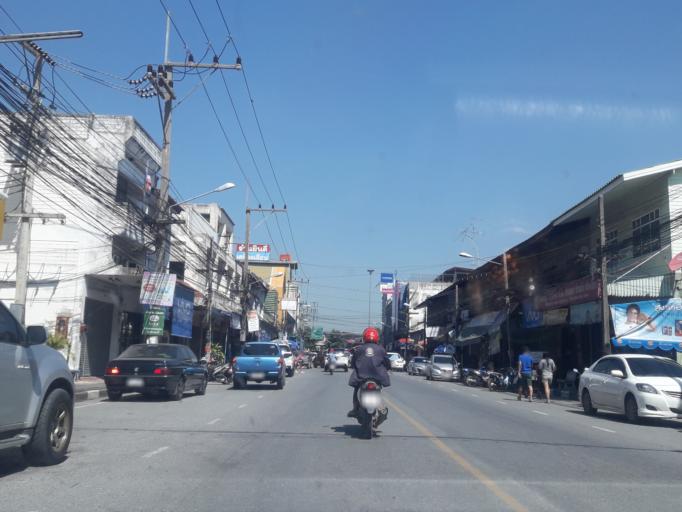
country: TH
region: Sara Buri
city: Nong Khae
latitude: 14.3452
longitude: 100.8669
